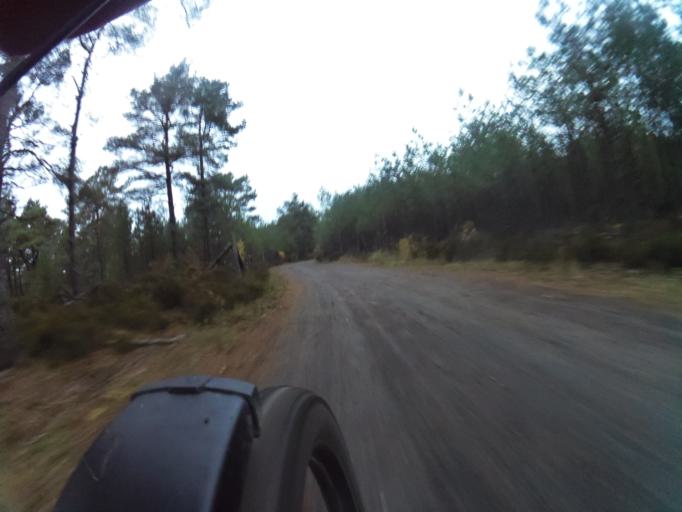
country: PL
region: Pomeranian Voivodeship
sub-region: Powiat wejherowski
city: Choczewo
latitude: 54.8001
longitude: 17.7825
